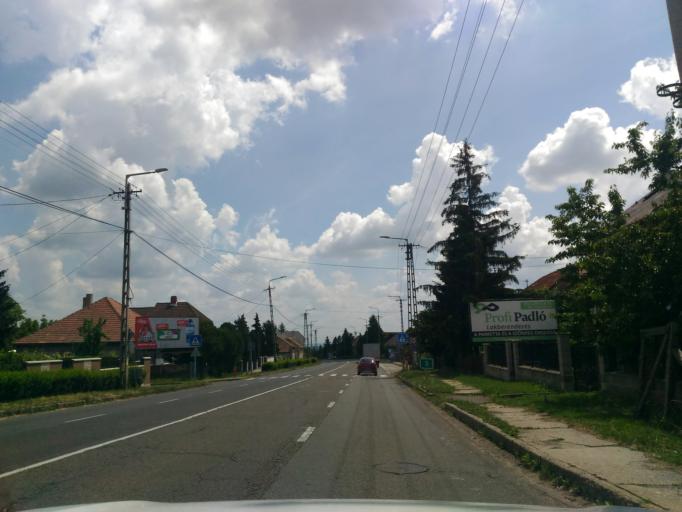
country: HU
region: Baranya
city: Pecs
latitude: 46.1128
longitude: 18.2620
